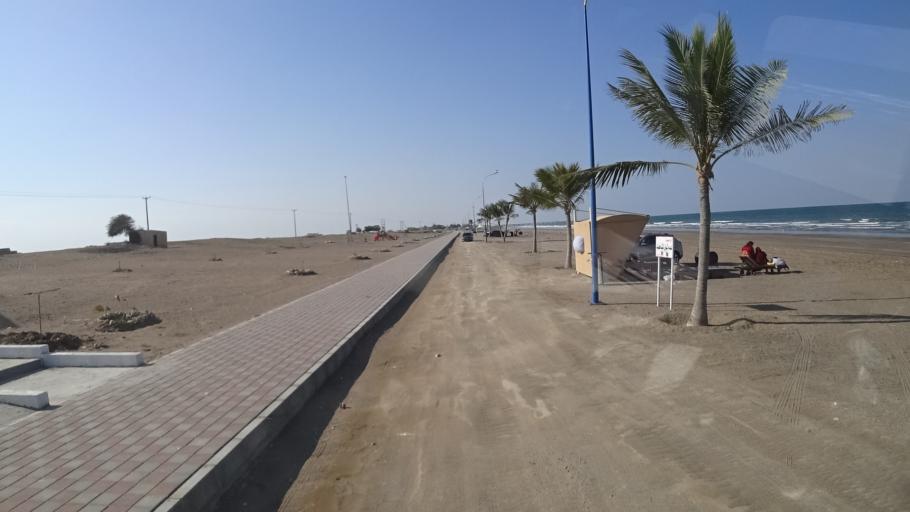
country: OM
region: Al Batinah
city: Al Khaburah
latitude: 23.9588
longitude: 57.1371
